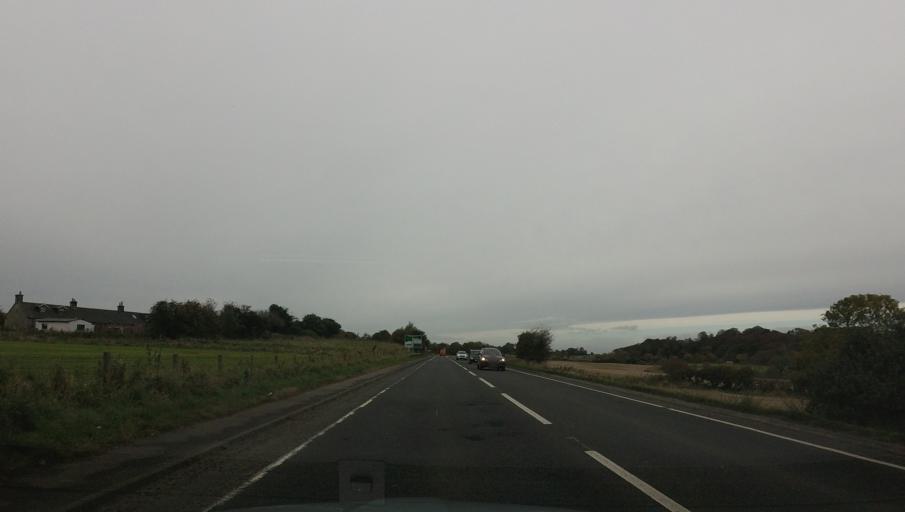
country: GB
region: Scotland
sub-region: Fife
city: Rosyth
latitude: 56.0354
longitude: -3.4538
